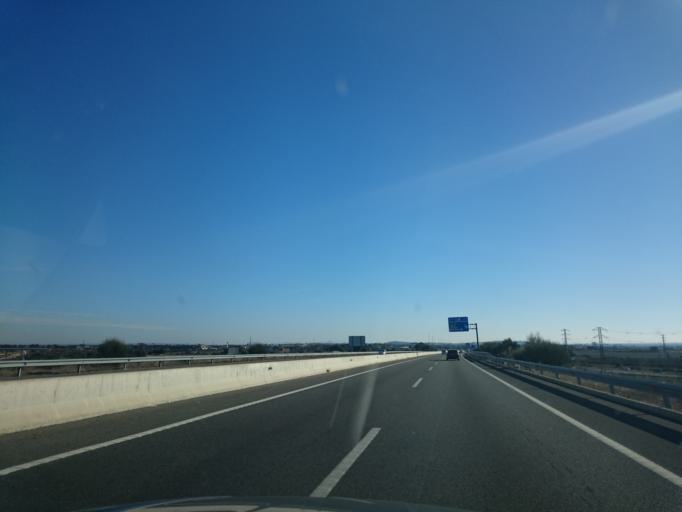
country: ES
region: Catalonia
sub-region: Provincia de Tarragona
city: Cambrils
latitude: 41.0848
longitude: 1.0612
